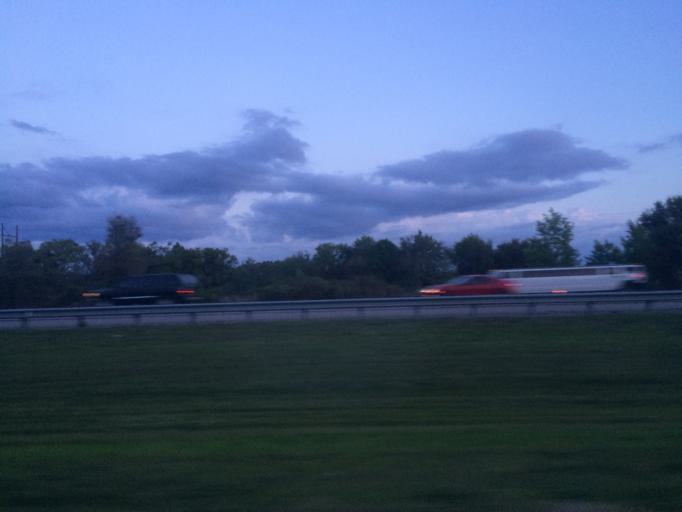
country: US
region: Florida
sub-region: Polk County
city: Loughman
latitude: 28.2720
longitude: -81.6028
